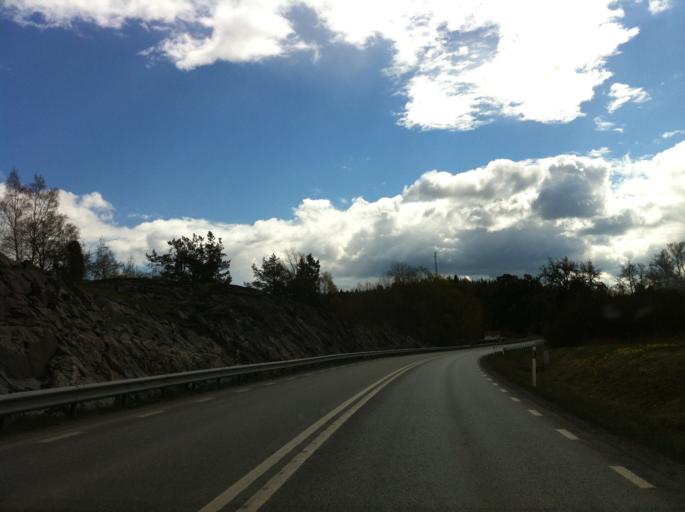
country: SE
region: Stockholm
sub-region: Taby Kommun
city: Taby
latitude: 59.4765
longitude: 18.1632
